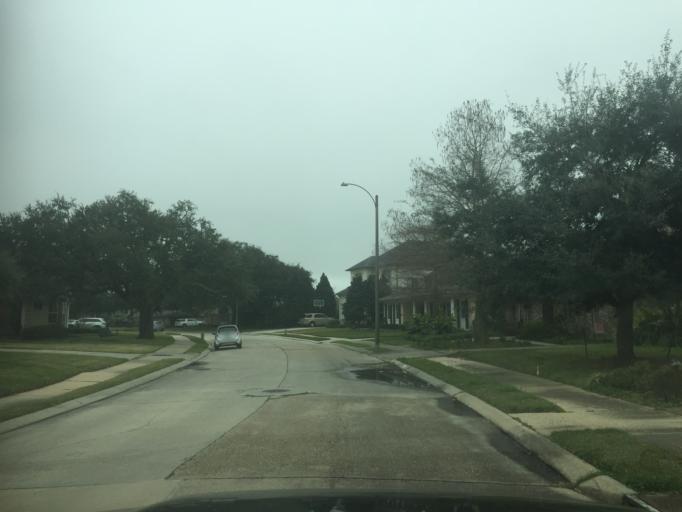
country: US
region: Louisiana
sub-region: Jefferson Parish
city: Metairie
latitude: 30.0206
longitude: -90.1045
